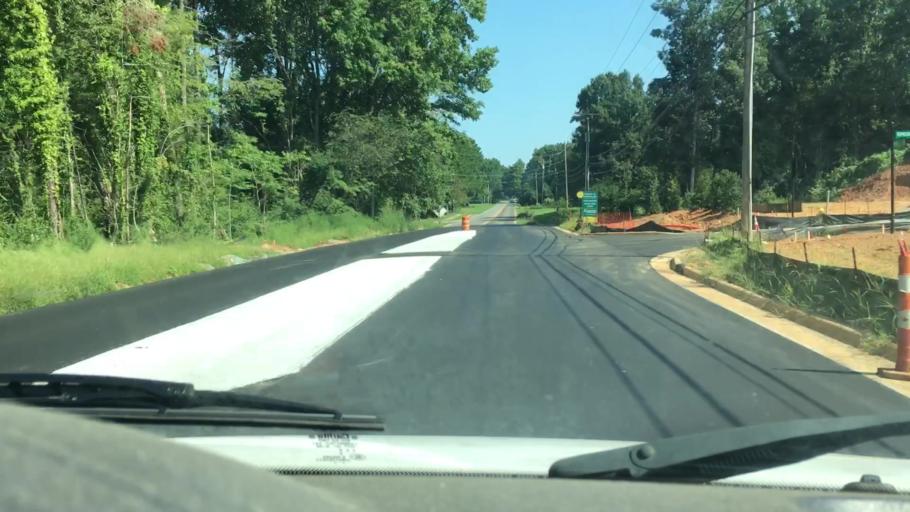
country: US
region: North Carolina
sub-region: Mecklenburg County
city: Huntersville
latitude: 35.3225
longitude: -80.8521
